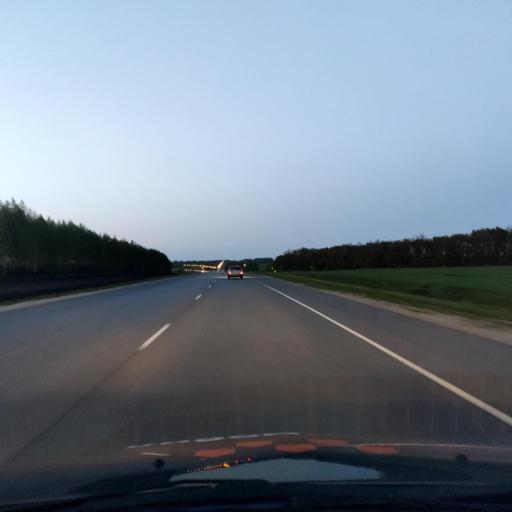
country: RU
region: Orjol
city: Zmiyevka
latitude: 52.7306
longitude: 36.3242
